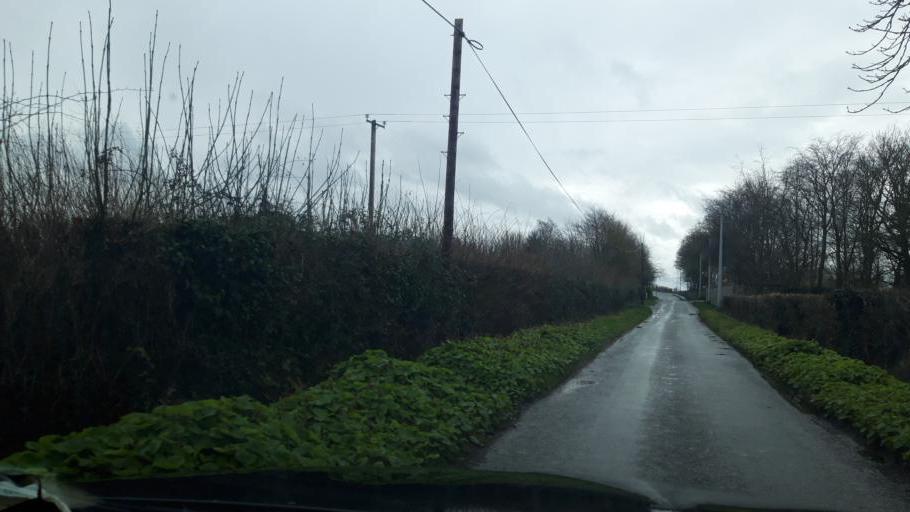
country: IE
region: Leinster
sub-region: Kildare
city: Leixlip
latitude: 53.3355
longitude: -6.4990
